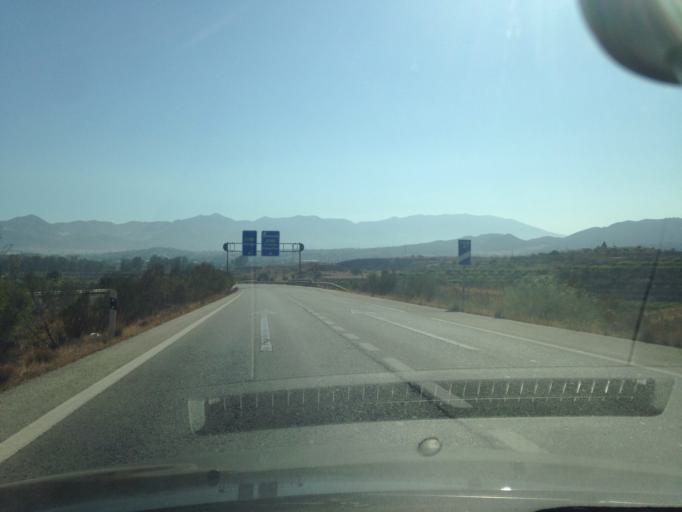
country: ES
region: Andalusia
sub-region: Provincia de Malaga
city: Alhaurin de la Torre
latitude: 36.7200
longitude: -4.5551
